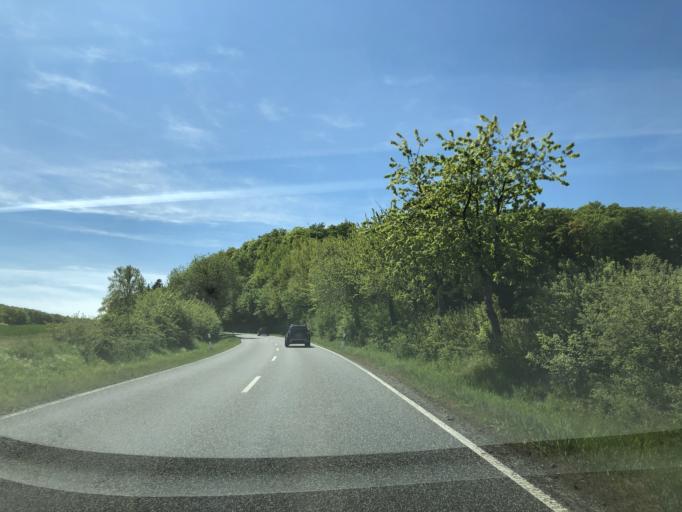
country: DE
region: Hesse
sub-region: Regierungsbezirk Kassel
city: Malsfeld
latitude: 51.0741
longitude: 9.4620
